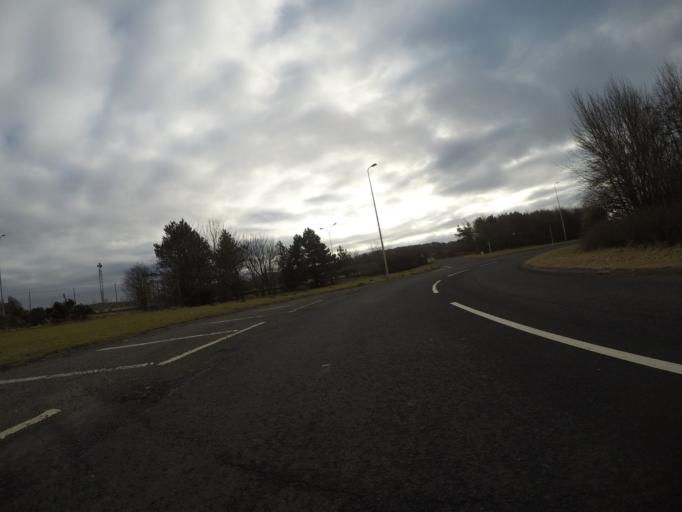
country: GB
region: Scotland
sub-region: North Ayrshire
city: Dreghorn
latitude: 55.5766
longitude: -4.6411
